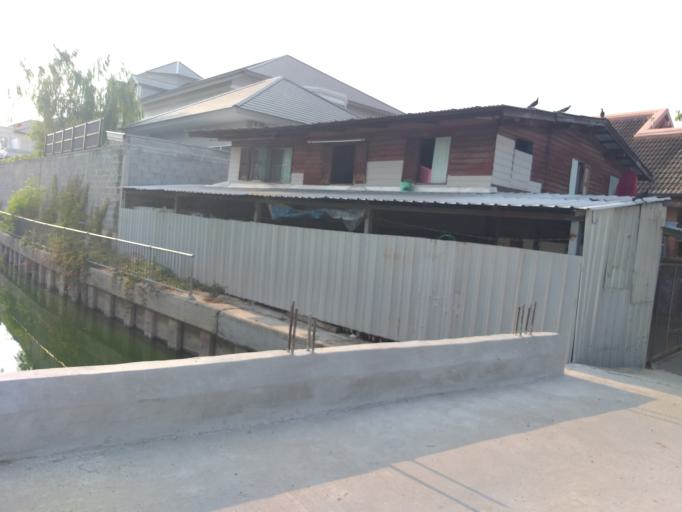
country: TH
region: Bangkok
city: Lat Phrao
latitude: 13.8226
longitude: 100.6146
